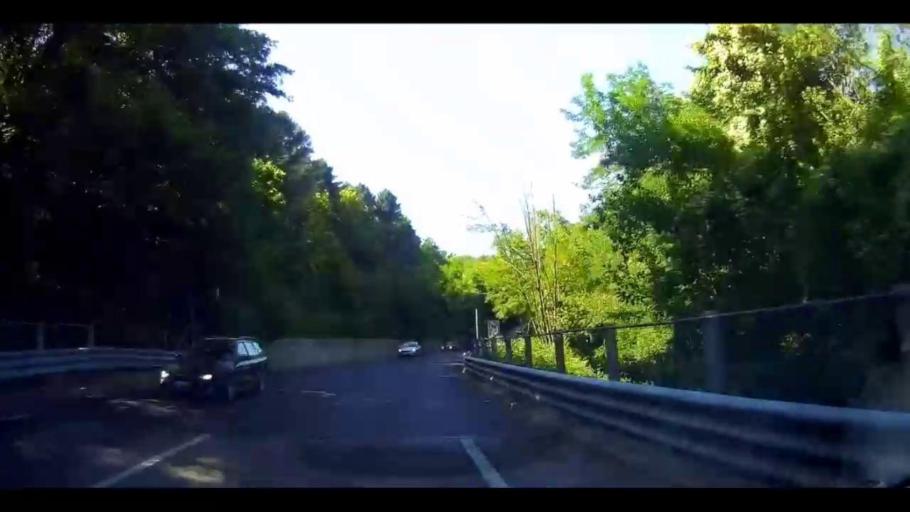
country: IT
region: Calabria
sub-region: Provincia di Cosenza
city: Spezzano Piccolo
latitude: 39.2994
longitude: 16.3561
